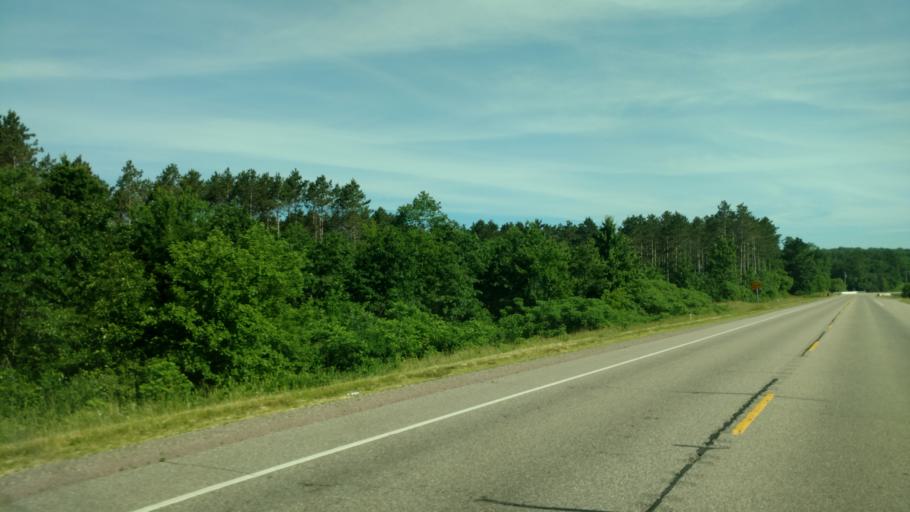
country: US
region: Wisconsin
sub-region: Sauk County
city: Lake Delton
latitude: 43.5555
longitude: -89.8422
